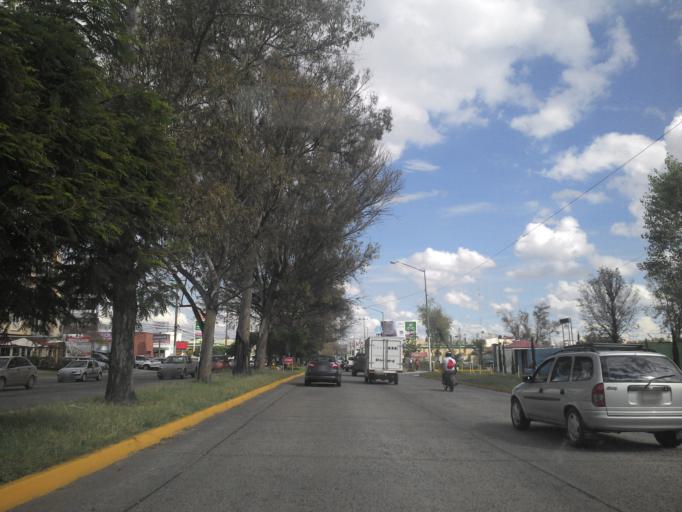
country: MX
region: Jalisco
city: Guadalajara
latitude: 20.6586
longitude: -103.4390
